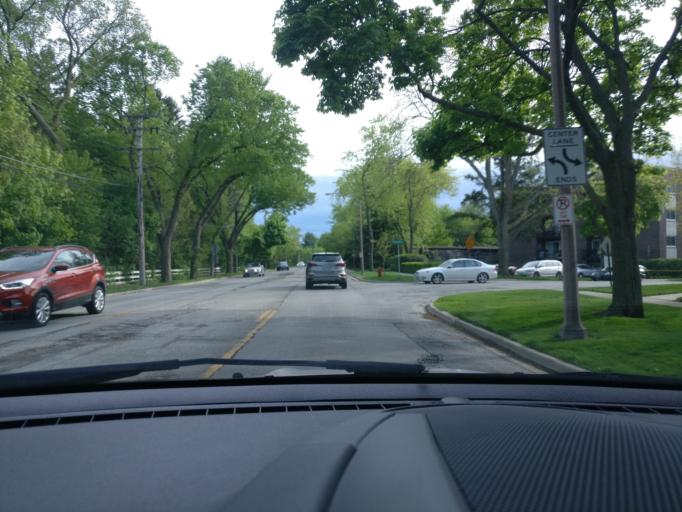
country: US
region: Illinois
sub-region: Cook County
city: Wilmette
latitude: 42.0702
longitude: -87.7229
